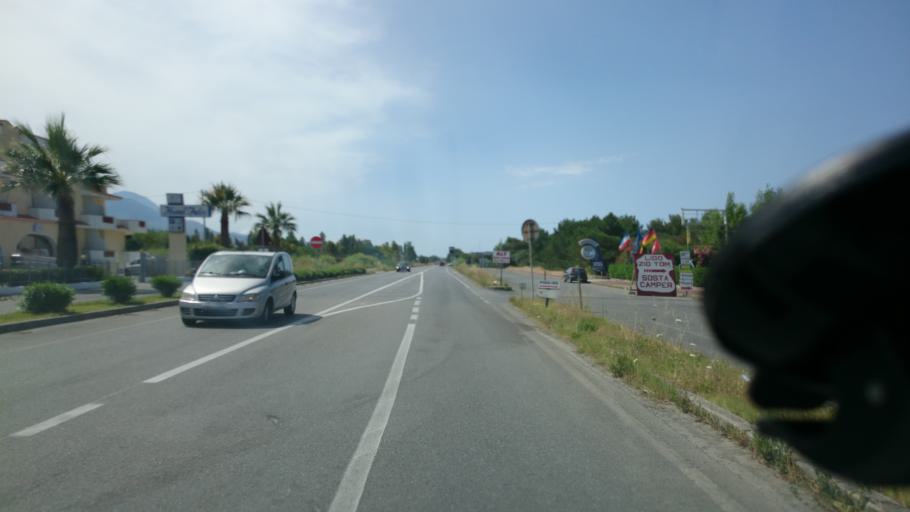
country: IT
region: Calabria
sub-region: Provincia di Cosenza
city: Scalea
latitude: 39.7965
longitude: 15.7927
